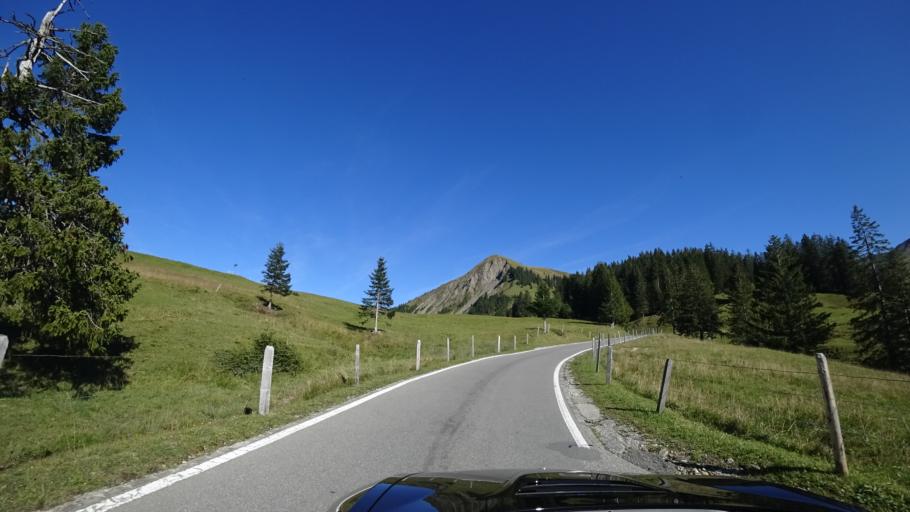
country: CH
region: Bern
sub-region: Interlaken-Oberhasli District
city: Brienz
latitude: 46.8184
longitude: 8.0831
